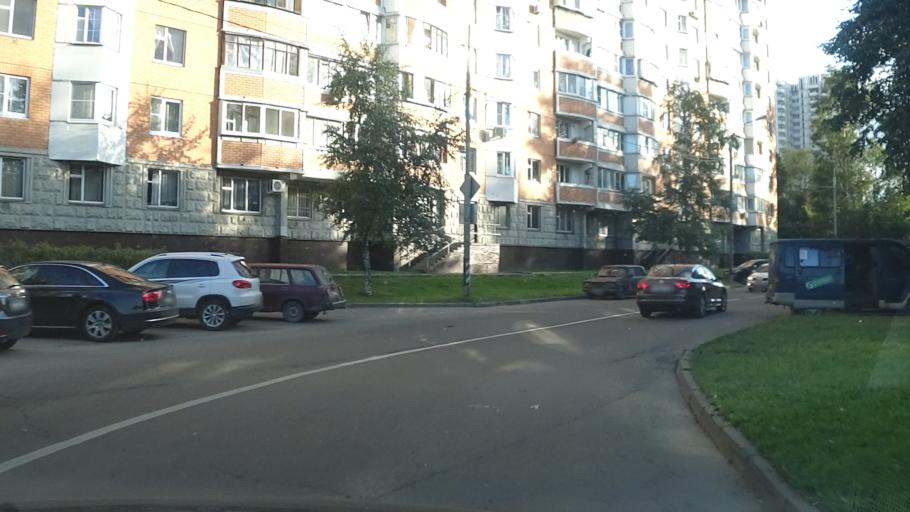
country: RU
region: Moscow
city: Solntsevo
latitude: 55.6542
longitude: 37.3962
